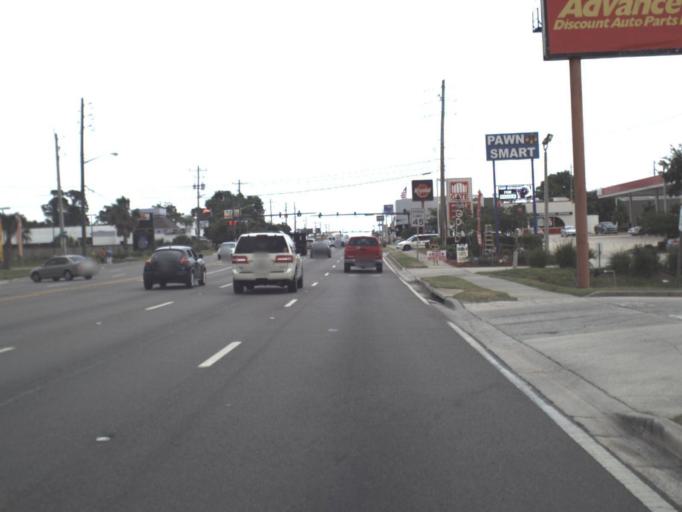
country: US
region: Florida
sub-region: Duval County
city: Jacksonville
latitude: 30.3226
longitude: -81.5401
